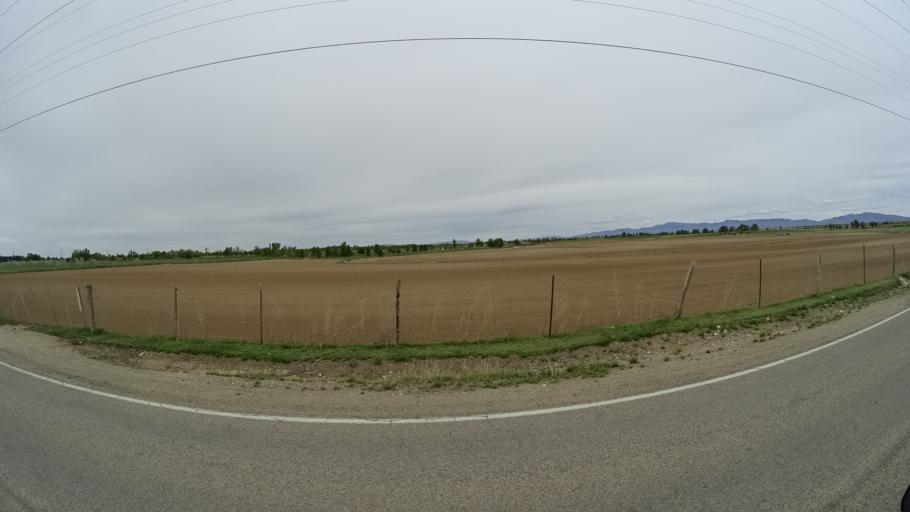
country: US
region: Idaho
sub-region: Ada County
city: Kuna
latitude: 43.4882
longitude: -116.3238
